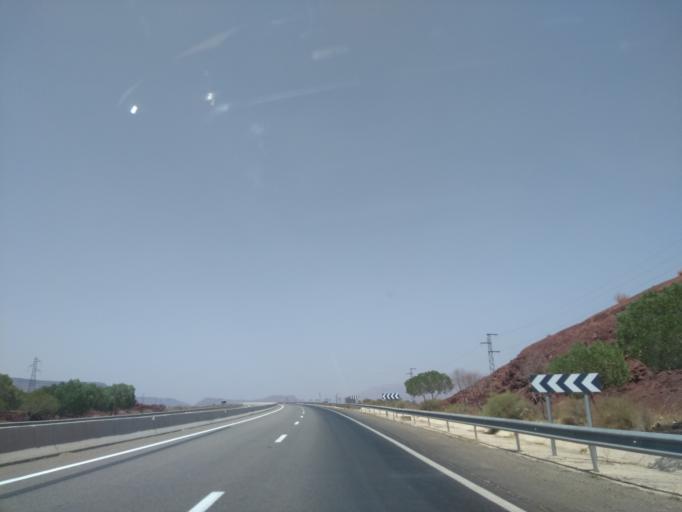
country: MA
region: Marrakech-Tensift-Al Haouz
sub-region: Chichaoua
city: Timezgadiouine
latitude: 30.8782
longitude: -9.0808
